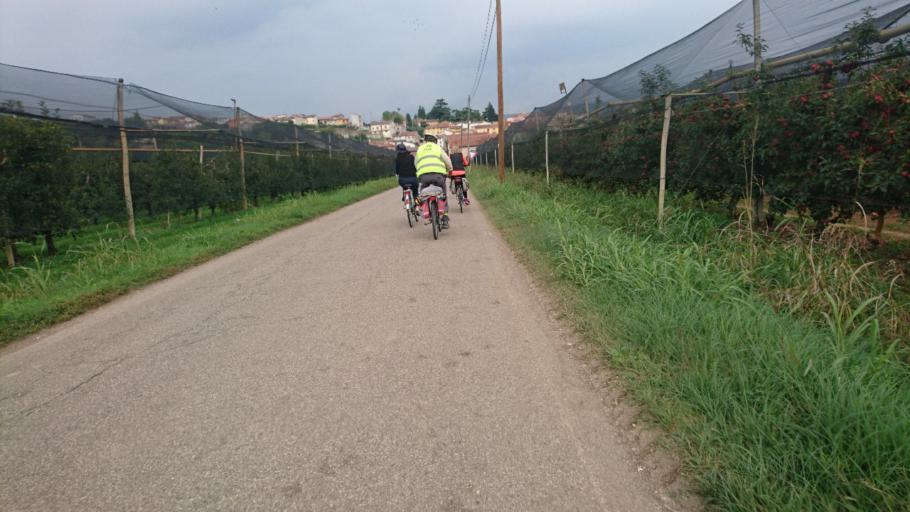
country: IT
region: Veneto
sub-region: Provincia di Verona
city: Soave
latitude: 45.4254
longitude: 11.2214
